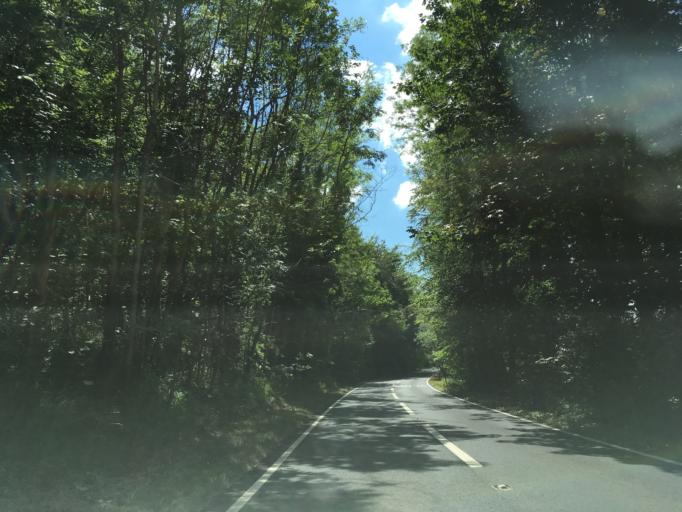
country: GB
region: England
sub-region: Gloucestershire
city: Painswick
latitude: 51.8055
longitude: -2.1951
